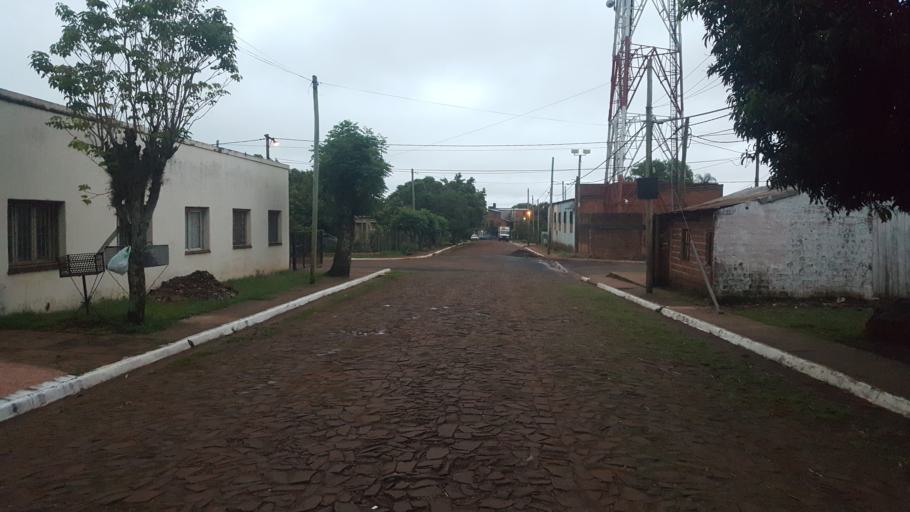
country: AR
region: Misiones
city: Garupa
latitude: -27.4578
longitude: -55.8599
